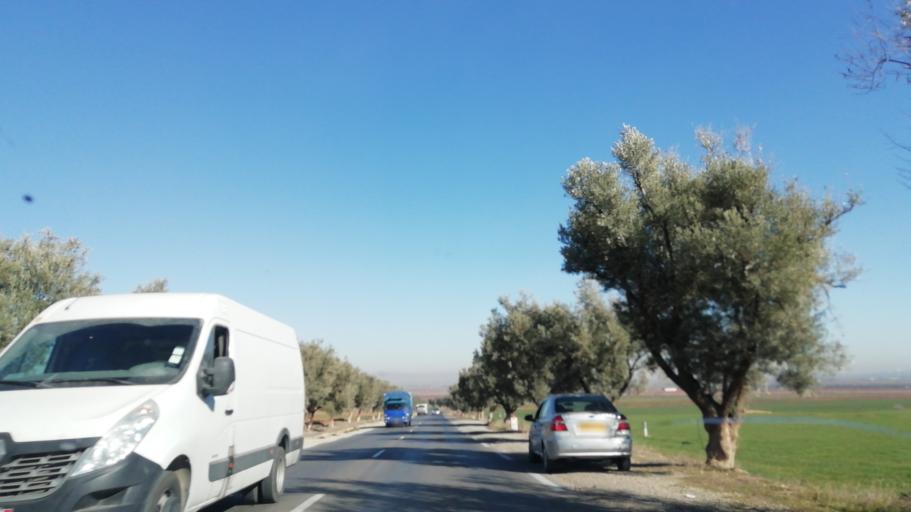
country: DZ
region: Mascara
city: Mascara
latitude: 35.2600
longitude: 0.1276
